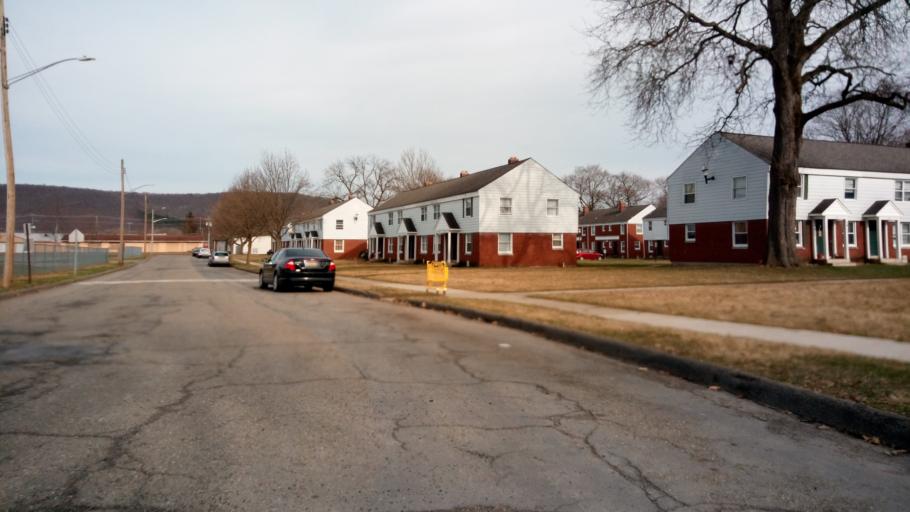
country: US
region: New York
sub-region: Chemung County
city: Elmira Heights
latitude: 42.1109
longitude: -76.8238
